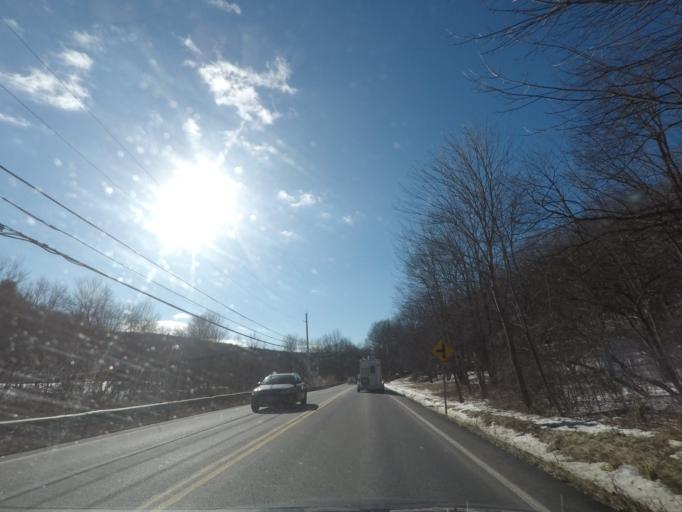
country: US
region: Massachusetts
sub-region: Berkshire County
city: Richmond
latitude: 42.4180
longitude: -73.4759
